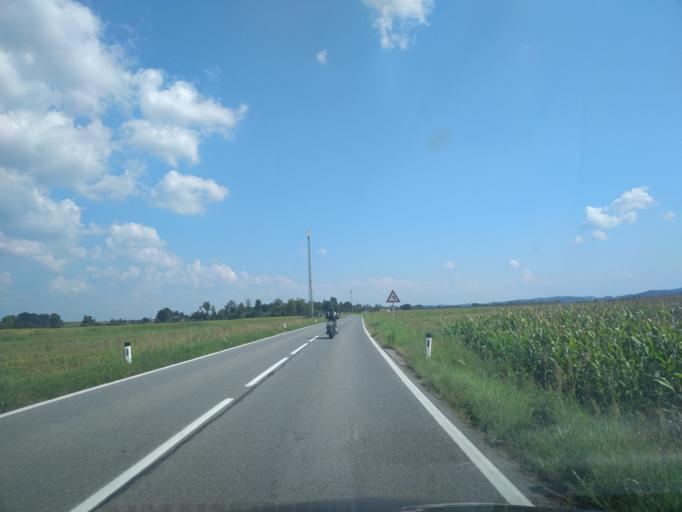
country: AT
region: Styria
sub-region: Politischer Bezirk Leibnitz
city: Gabersdorf
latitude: 46.7625
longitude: 15.5850
